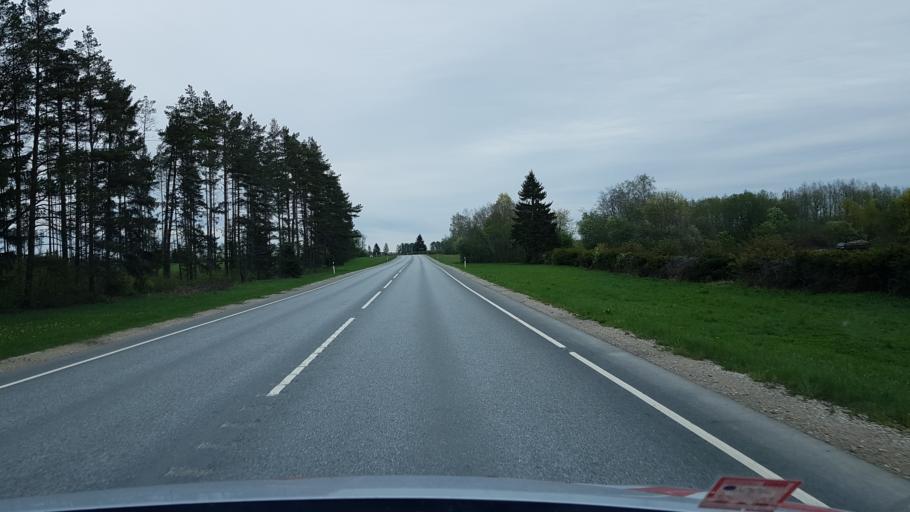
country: EE
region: Laeaene-Virumaa
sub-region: Tapa vald
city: Tapa
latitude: 59.2866
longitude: 26.0454
